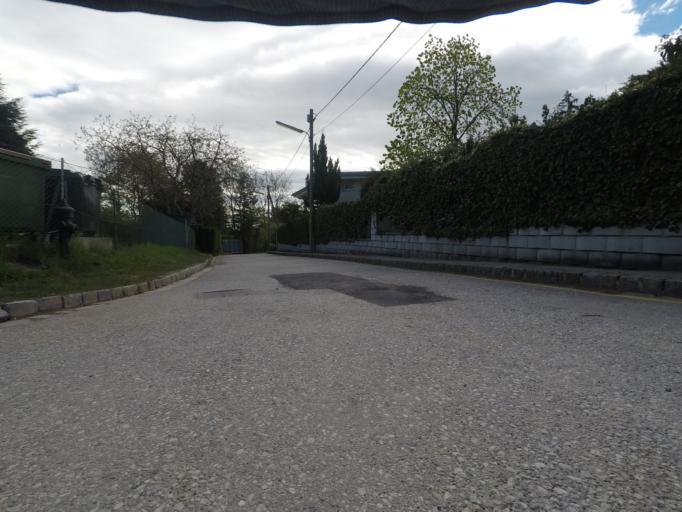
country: AT
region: Lower Austria
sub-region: Politischer Bezirk Modling
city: Perchtoldsdorf
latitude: 48.1747
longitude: 16.2543
